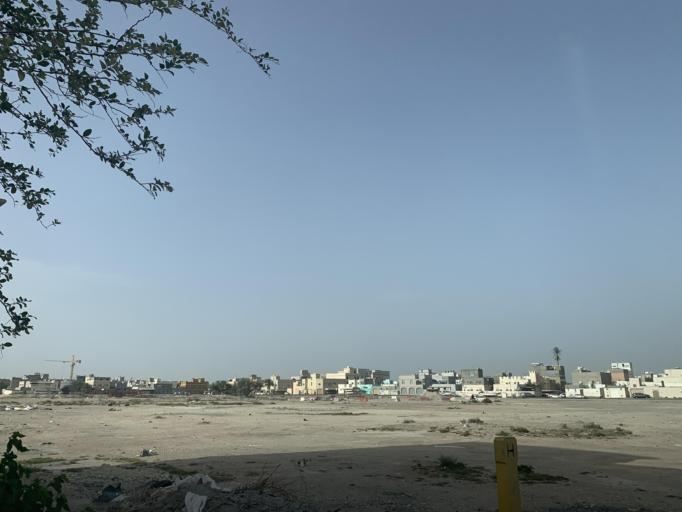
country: BH
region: Northern
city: Madinat `Isa
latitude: 26.1596
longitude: 50.5088
